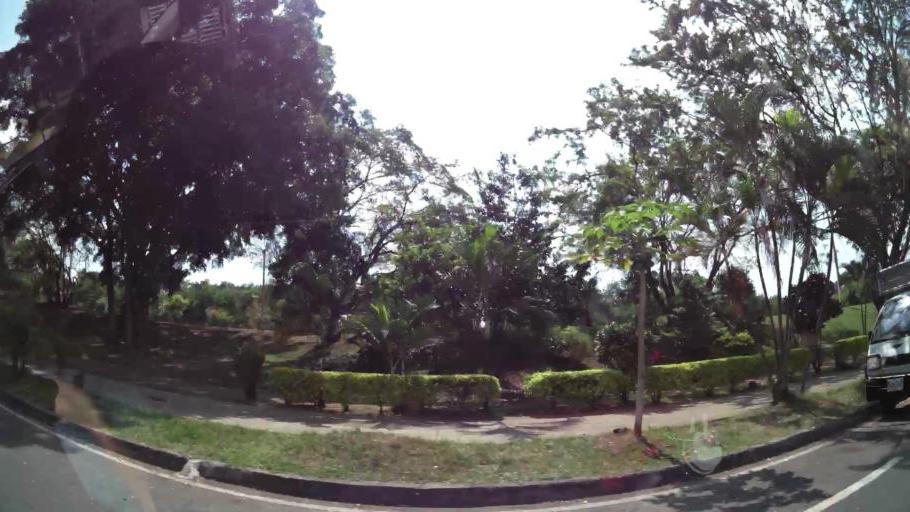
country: CO
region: Valle del Cauca
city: Cali
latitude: 3.4929
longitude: -76.5012
